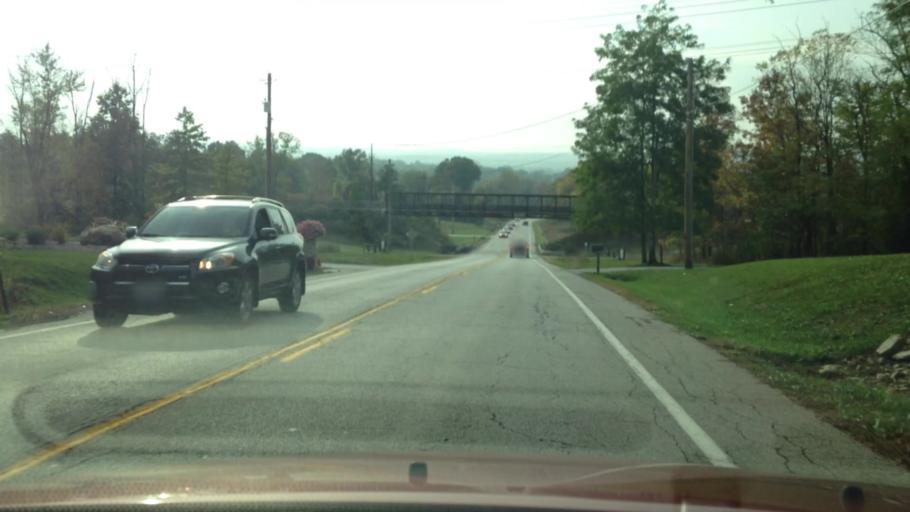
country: US
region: Ohio
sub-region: Cuyahoga County
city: Walton Hills
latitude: 41.3399
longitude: -81.5698
